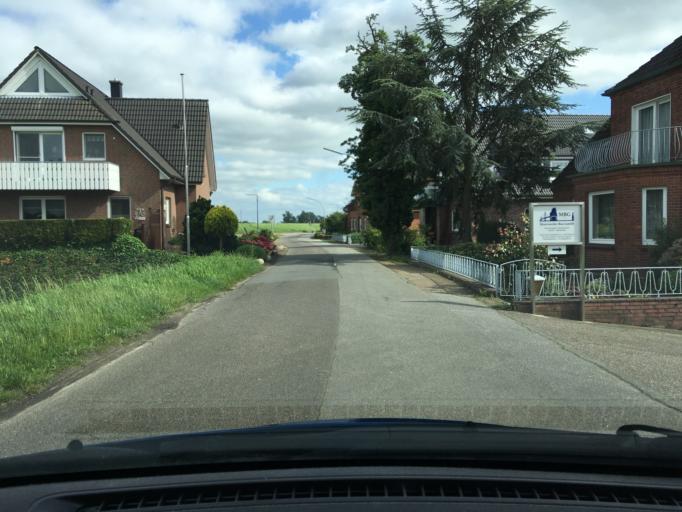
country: DE
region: Hamburg
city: Rothenburgsort
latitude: 53.4744
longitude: 10.0591
